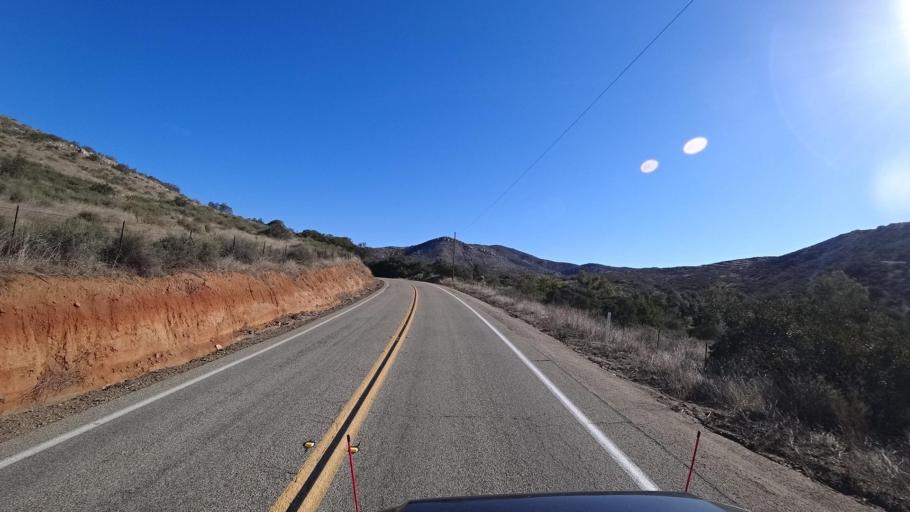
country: US
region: California
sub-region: San Diego County
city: Jamul
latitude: 32.6684
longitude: -116.8140
